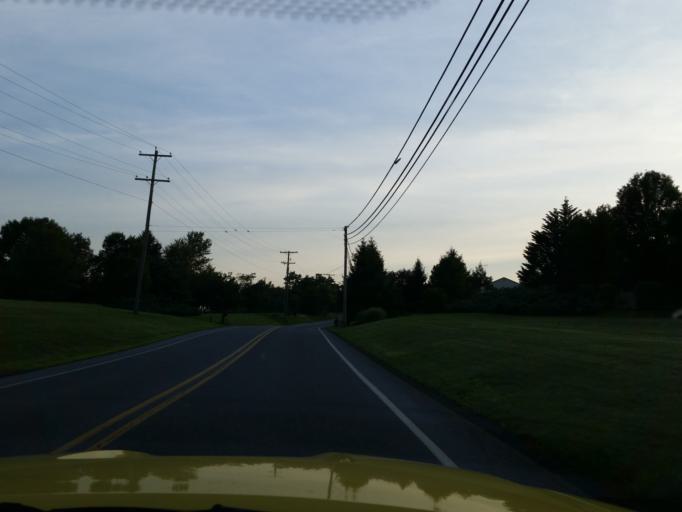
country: US
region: Pennsylvania
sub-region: Lebanon County
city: Jonestown
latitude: 40.4157
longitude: -76.4654
